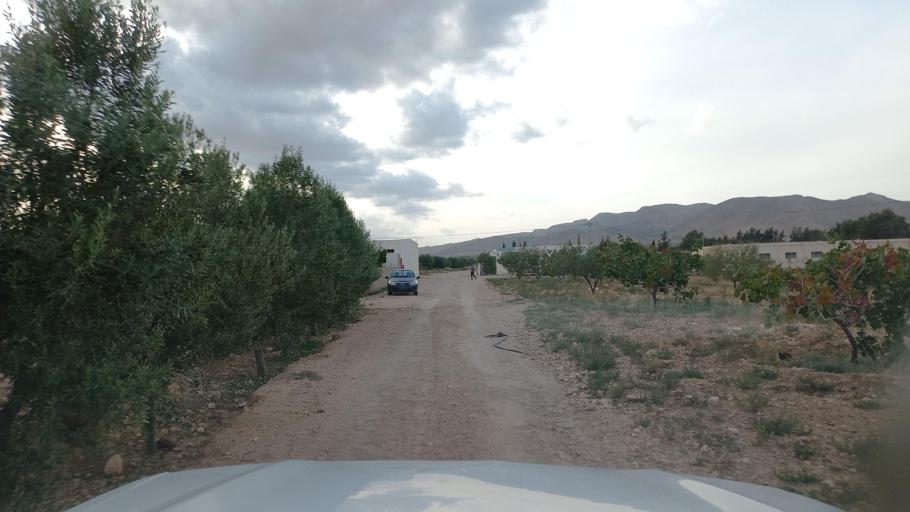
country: TN
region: Al Qasrayn
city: Sbiba
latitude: 35.4398
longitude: 9.0967
